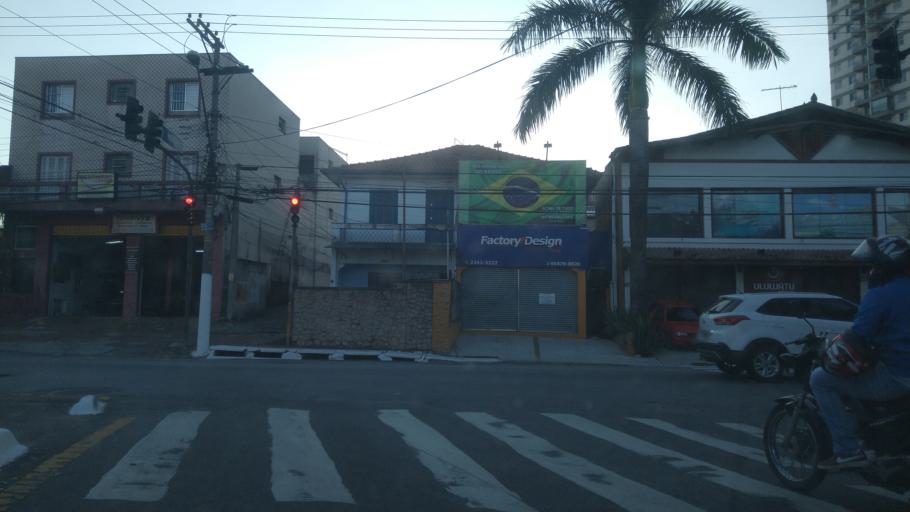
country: BR
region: Sao Paulo
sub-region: Sao Paulo
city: Sao Paulo
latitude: -23.4785
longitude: -46.6211
